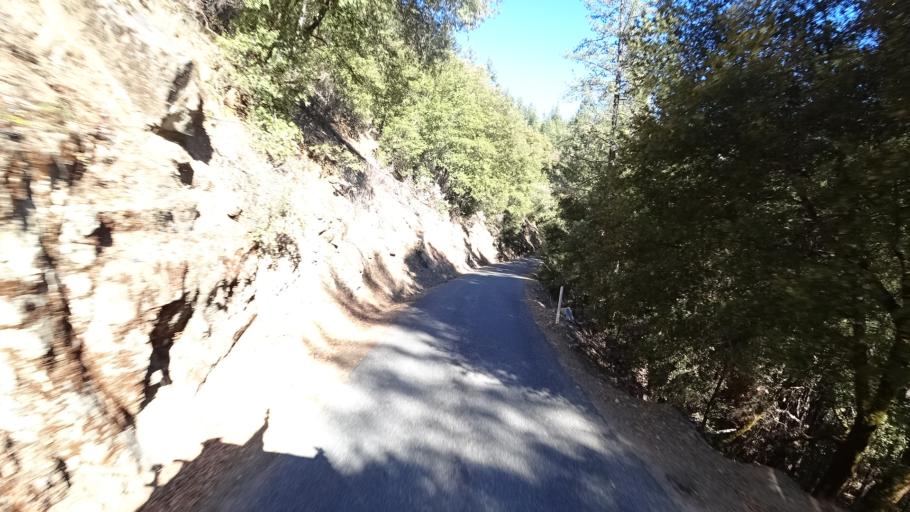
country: US
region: California
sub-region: Siskiyou County
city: Happy Camp
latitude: 41.2954
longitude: -123.2413
